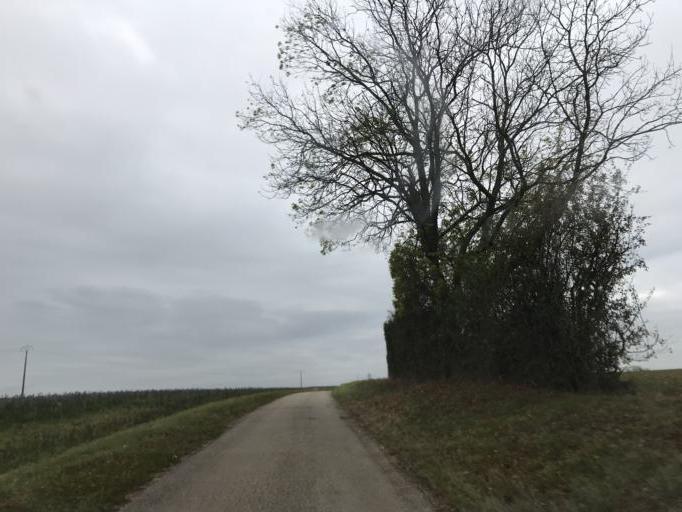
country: FR
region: Rhone-Alpes
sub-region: Departement de l'Ain
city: Saint-Maurice-de-Beynost
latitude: 45.8413
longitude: 4.9690
